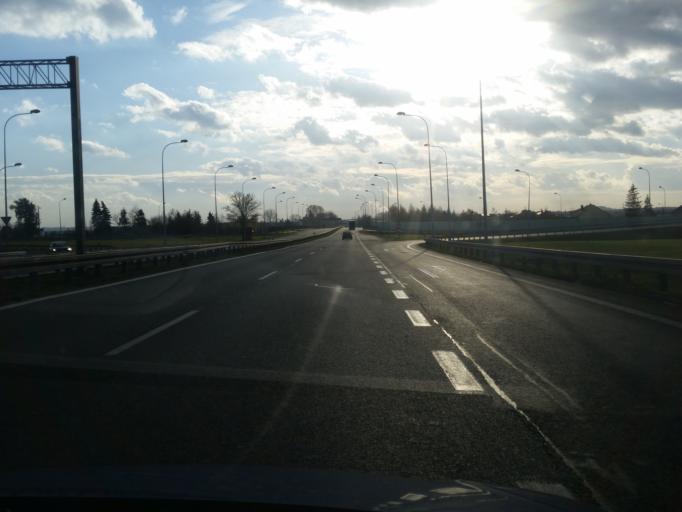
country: PL
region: Silesian Voivodeship
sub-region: Powiat bedzinski
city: Siewierz
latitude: 50.4196
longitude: 19.2103
